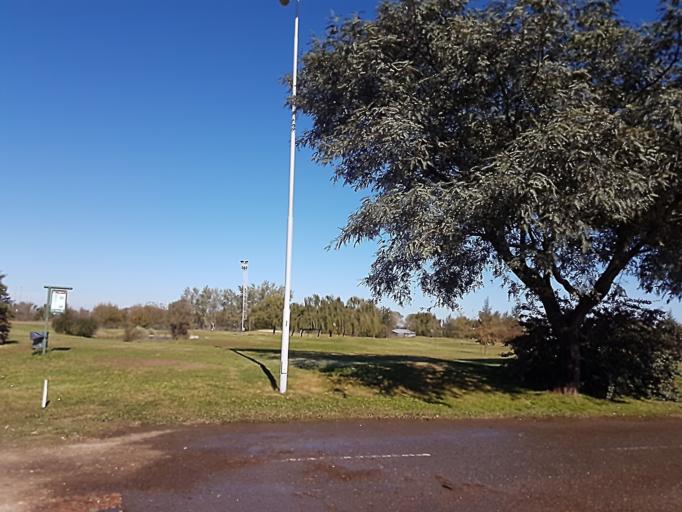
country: AR
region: Cordoba
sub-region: Departamento de Capital
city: Cordoba
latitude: -31.3370
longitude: -64.2026
